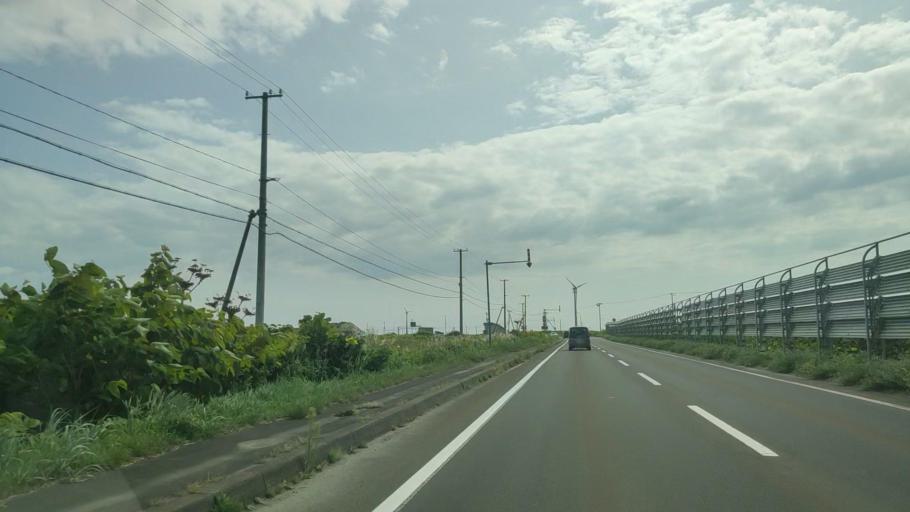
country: JP
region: Hokkaido
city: Rumoi
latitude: 44.2702
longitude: 141.6560
